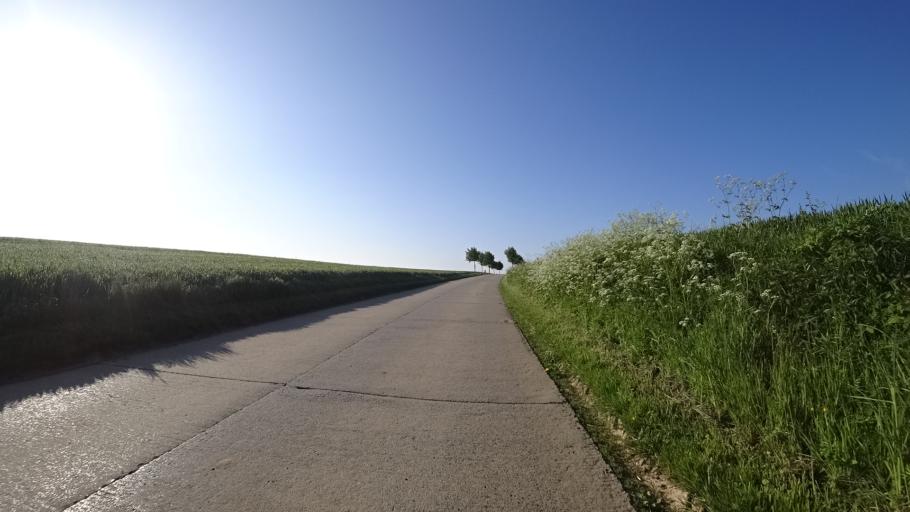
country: BE
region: Wallonia
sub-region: Province du Brabant Wallon
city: Walhain-Saint-Paul
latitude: 50.6293
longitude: 4.6860
